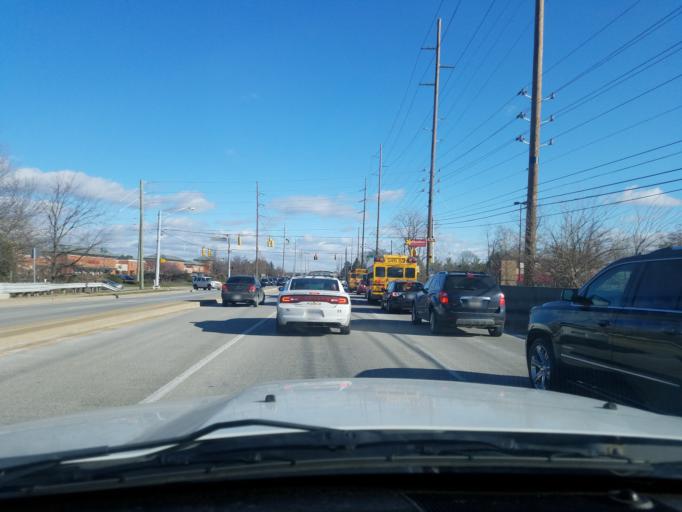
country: US
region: Indiana
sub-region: Marion County
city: Meridian Hills
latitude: 39.9117
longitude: -86.2146
